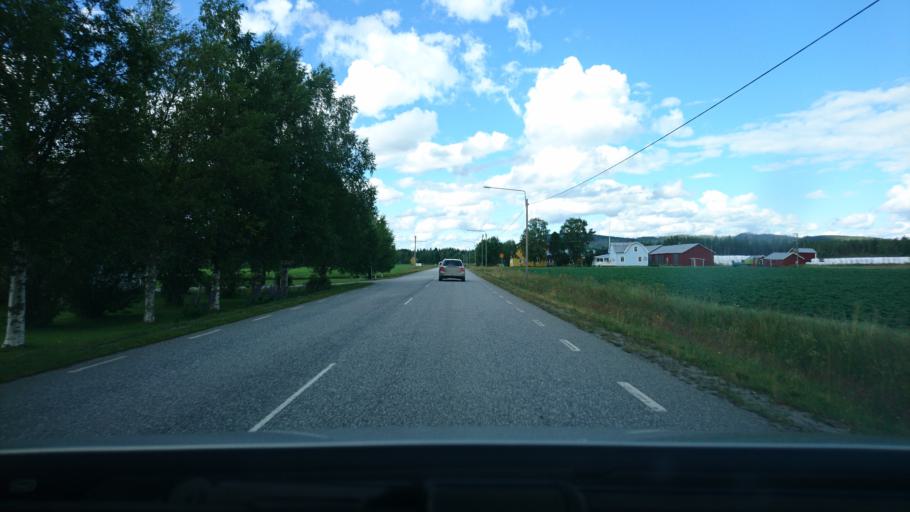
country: SE
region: Vaesterbotten
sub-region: Asele Kommun
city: Asele
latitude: 64.0189
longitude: 17.2961
